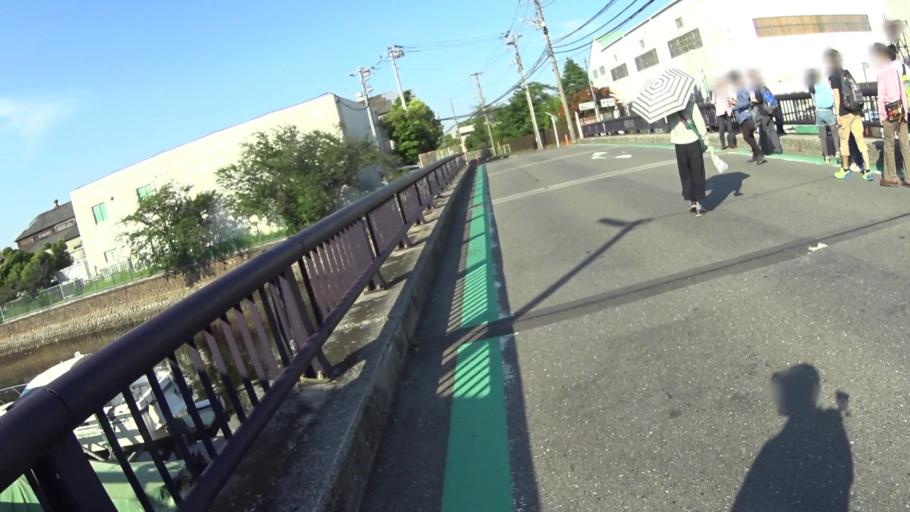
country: JP
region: Kanagawa
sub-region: Kawasaki-shi
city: Kawasaki
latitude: 35.4988
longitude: 139.6959
